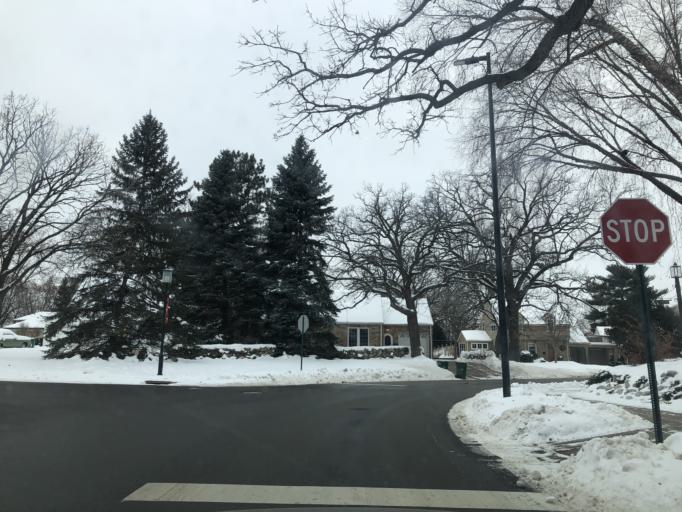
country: US
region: Minnesota
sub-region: Hennepin County
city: Robbinsdale
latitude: 45.0278
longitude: -93.3223
